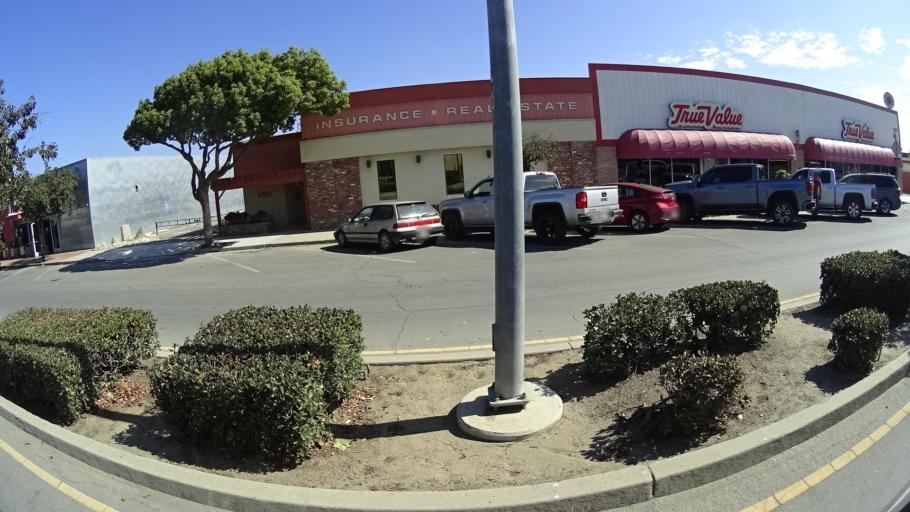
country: US
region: California
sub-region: Monterey County
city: Greenfield
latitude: 36.3203
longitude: -121.2430
